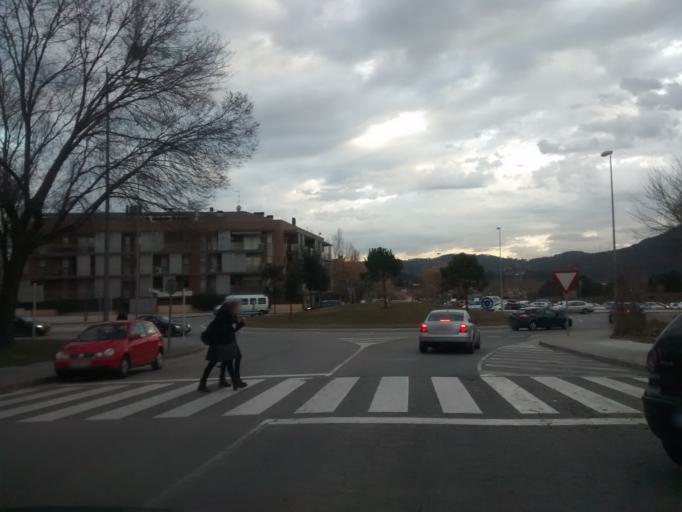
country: ES
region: Catalonia
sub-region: Provincia de Barcelona
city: Rubi
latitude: 41.4739
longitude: 2.0418
